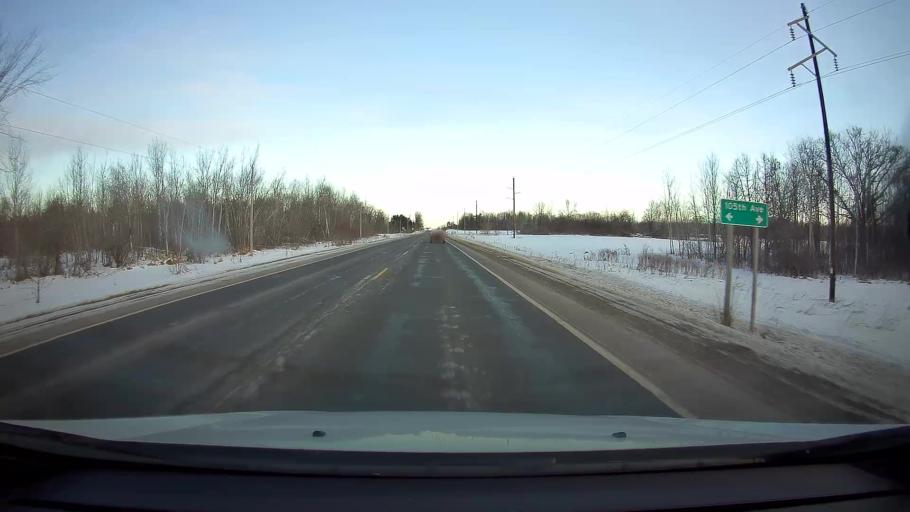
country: US
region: Wisconsin
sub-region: Barron County
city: Turtle Lake
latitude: 45.3575
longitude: -92.1668
